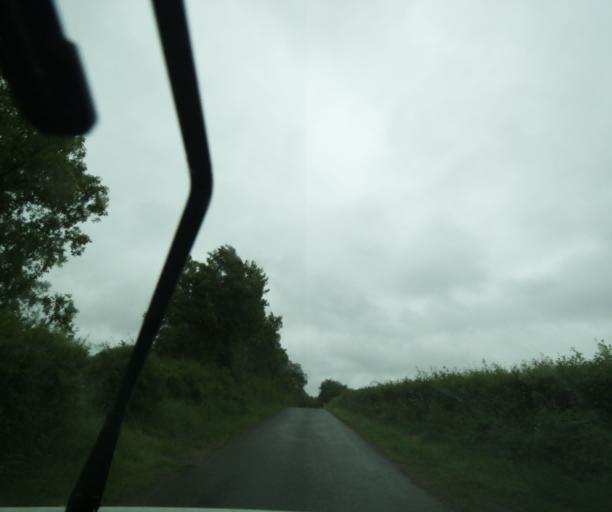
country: FR
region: Bourgogne
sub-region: Departement de Saone-et-Loire
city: Palinges
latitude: 46.5257
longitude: 4.2200
